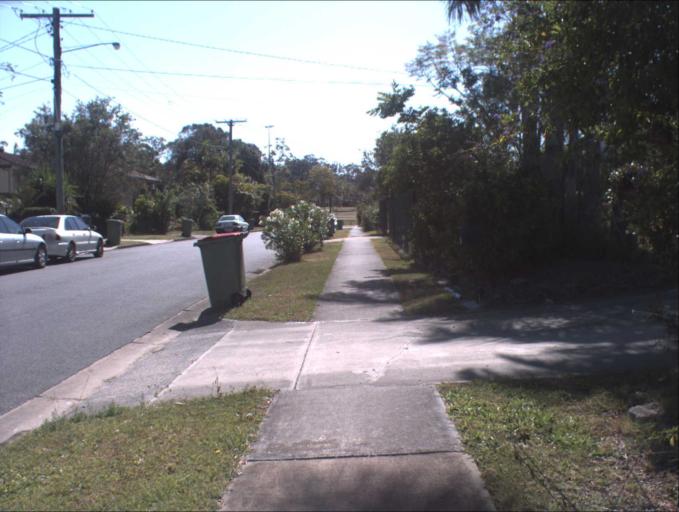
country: AU
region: Queensland
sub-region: Logan
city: Logan City
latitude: -27.6461
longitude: 153.1006
